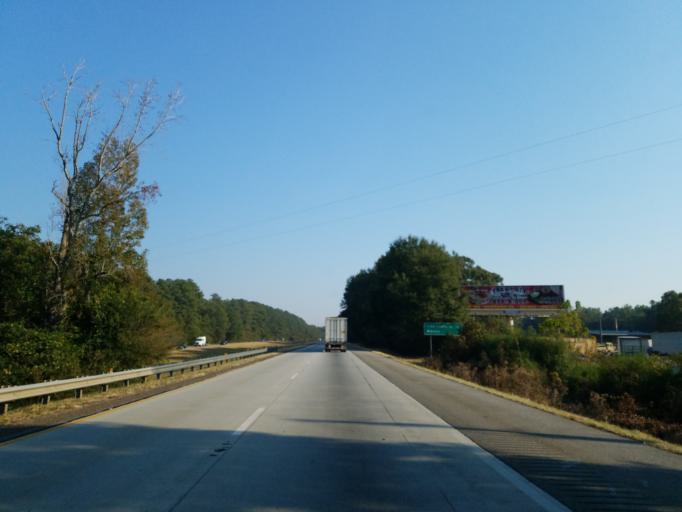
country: US
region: Georgia
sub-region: Monroe County
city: Forsyth
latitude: 32.9546
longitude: -83.8089
